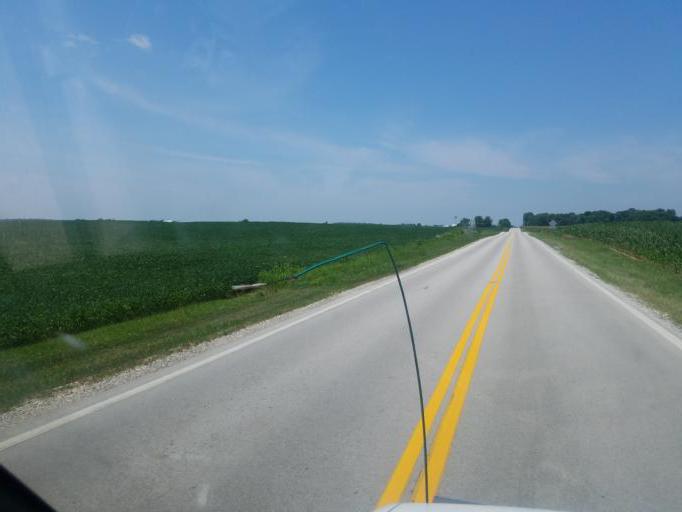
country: US
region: Ohio
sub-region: Auglaize County
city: New Bremen
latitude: 40.4224
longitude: -84.4337
